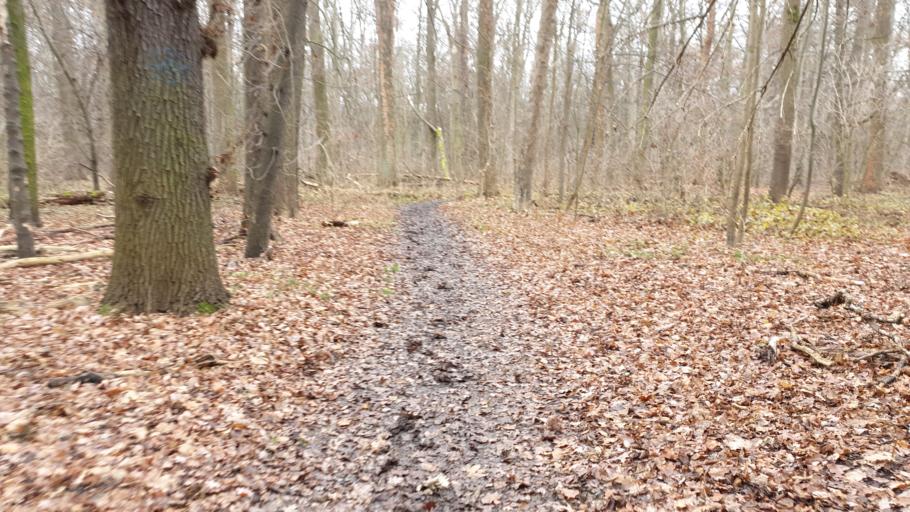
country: DE
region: Saxony
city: Schkeuditz
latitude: 51.3683
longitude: 12.2877
